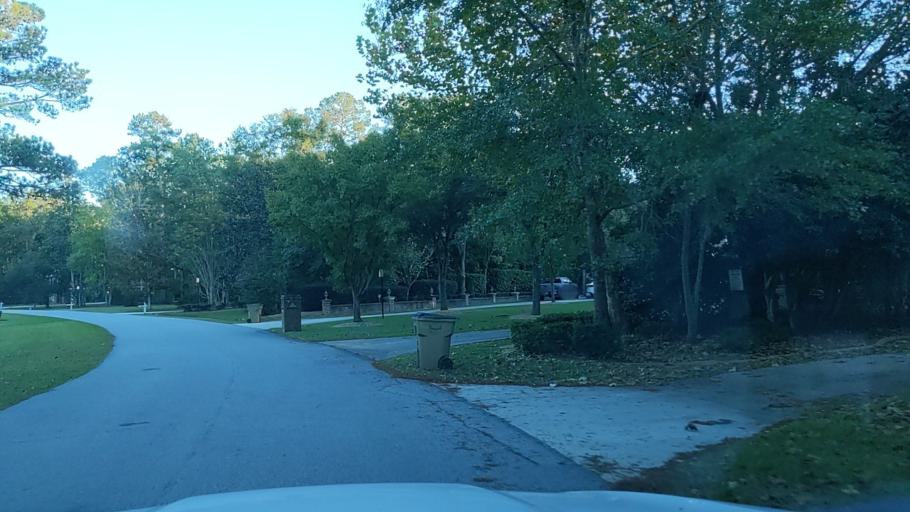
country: US
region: Georgia
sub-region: Effingham County
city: Rincon
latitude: 32.2627
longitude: -81.2174
